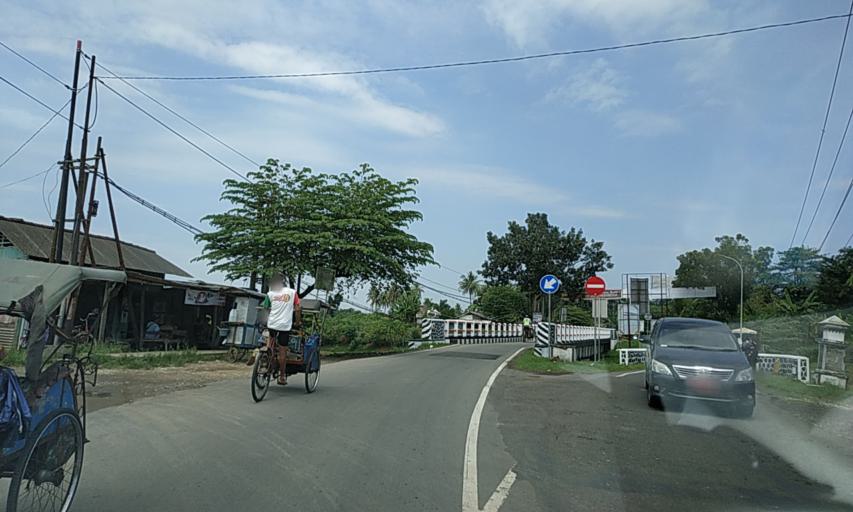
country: ID
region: Central Java
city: Sidareja
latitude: -7.4900
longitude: 108.7915
